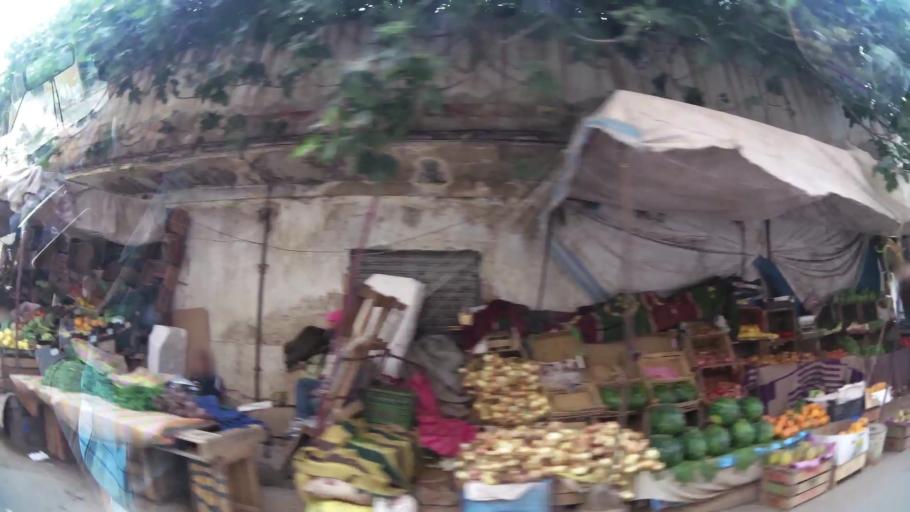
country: MA
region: Oriental
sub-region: Nador
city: Nador
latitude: 35.1682
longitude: -2.9418
